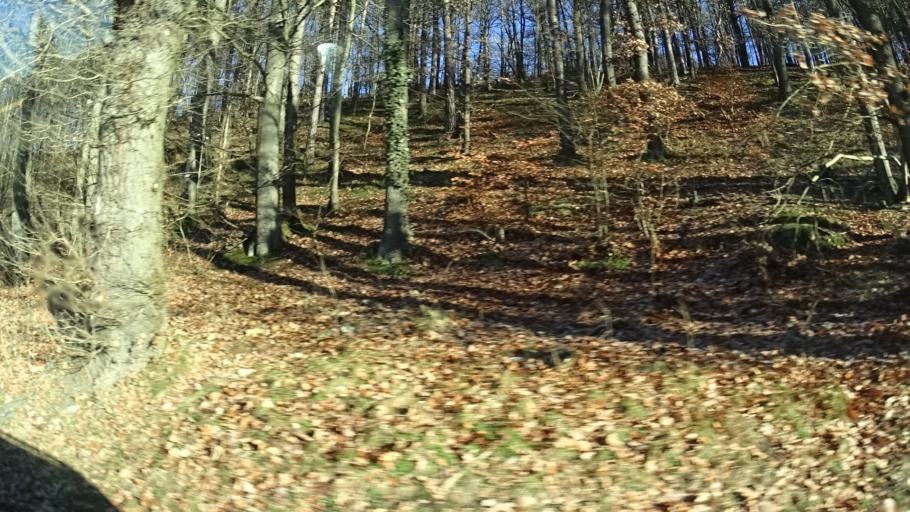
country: DE
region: Thuringia
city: Kleineutersdorf
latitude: 50.7882
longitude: 11.5860
